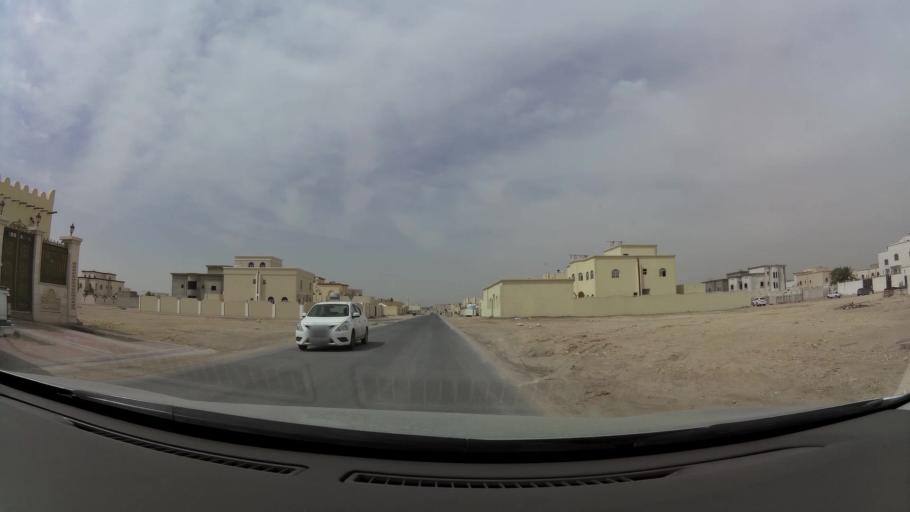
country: QA
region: Baladiyat ar Rayyan
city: Ar Rayyan
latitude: 25.2133
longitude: 51.4565
